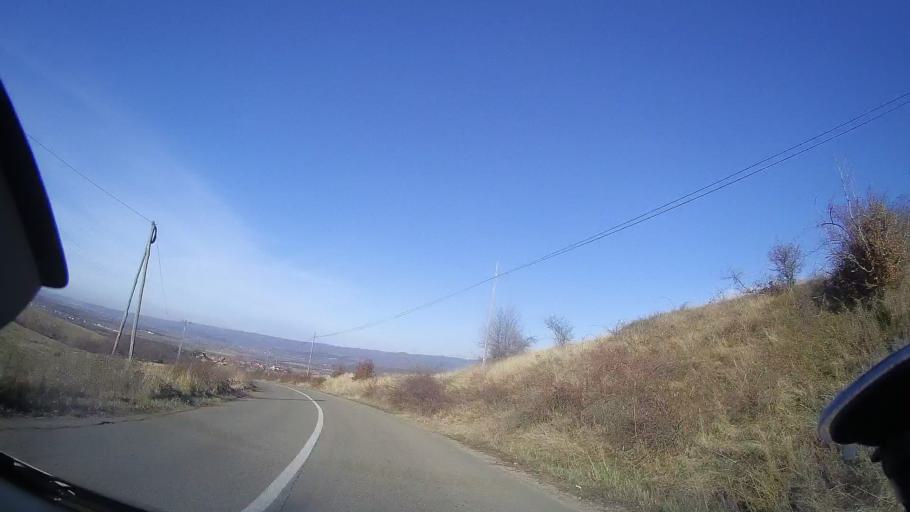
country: RO
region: Bihor
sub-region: Comuna Vadu Crisului
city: Vadu Crisului
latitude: 46.9773
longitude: 22.5342
